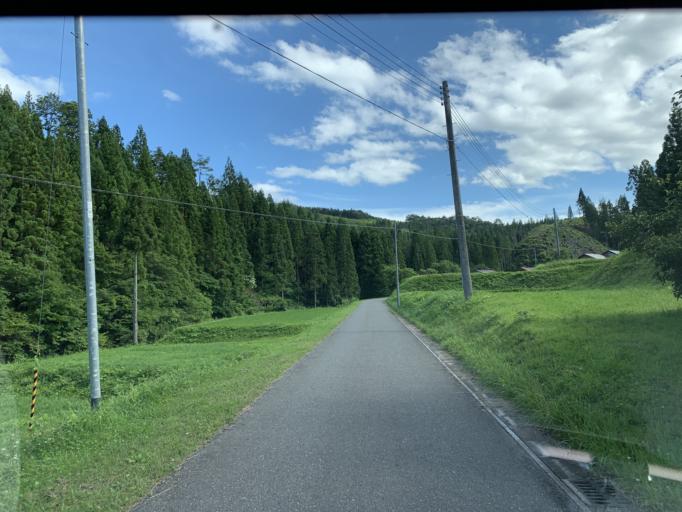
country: JP
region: Iwate
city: Ichinoseki
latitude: 38.9223
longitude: 140.9412
